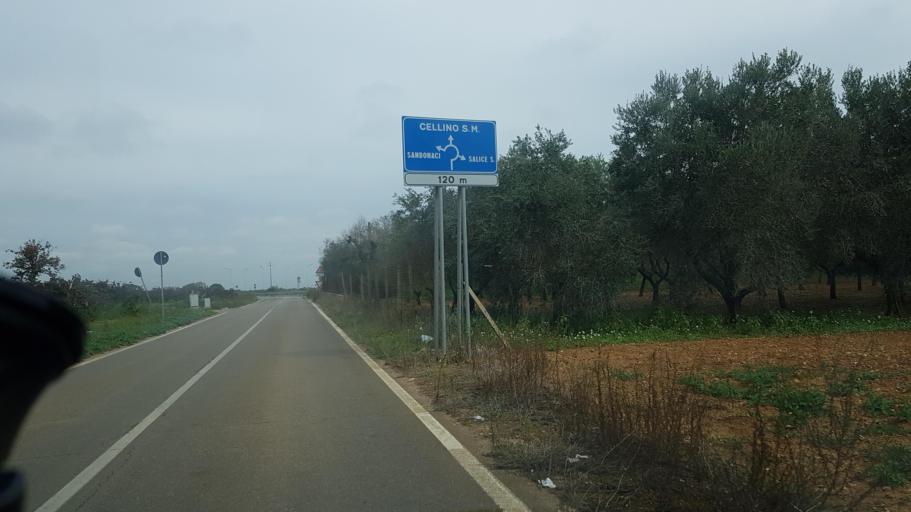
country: IT
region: Apulia
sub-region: Provincia di Lecce
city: Guagnano
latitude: 40.4194
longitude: 17.9499
